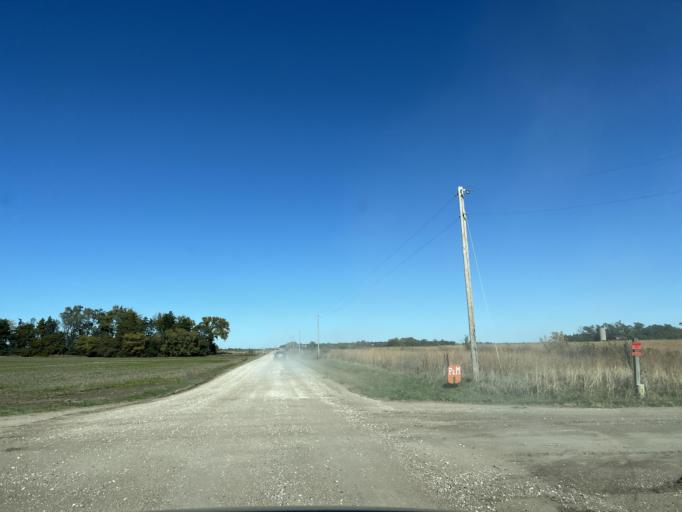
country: US
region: Kansas
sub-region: McPherson County
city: Moundridge
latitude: 38.2176
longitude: -97.6292
